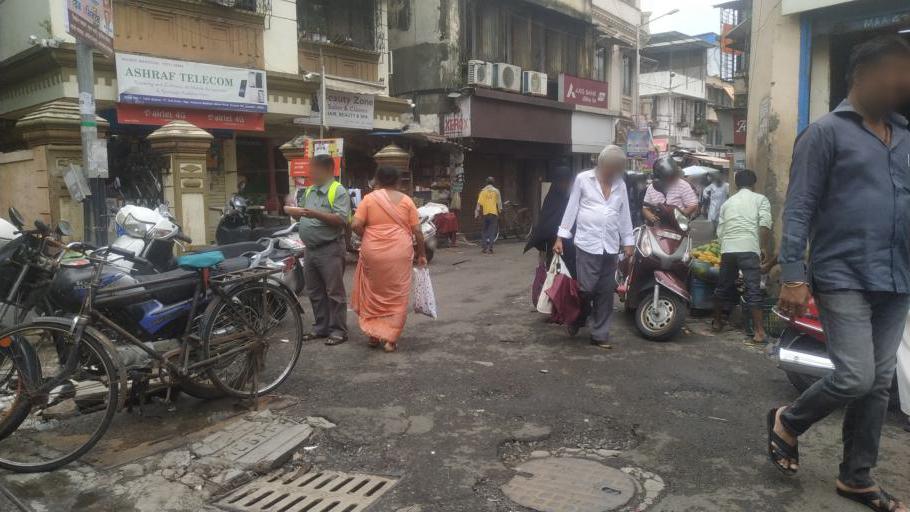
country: IN
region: Maharashtra
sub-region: Mumbai Suburban
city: Mumbai
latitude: 19.0542
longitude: 72.8333
